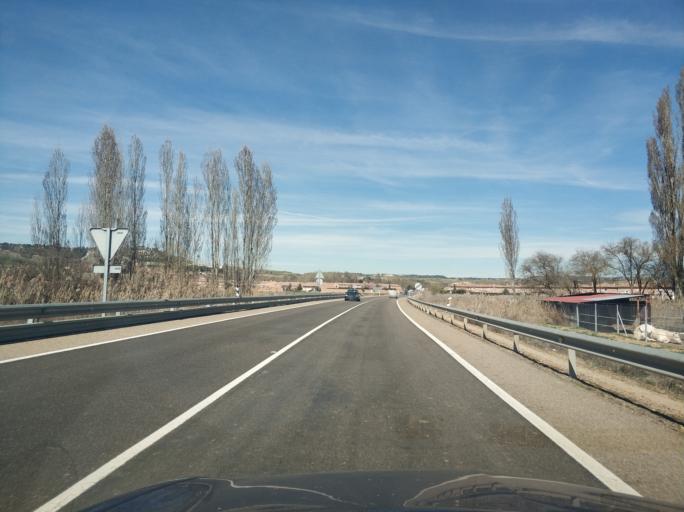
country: ES
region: Castille and Leon
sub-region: Provincia de Valladolid
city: Simancas
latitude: 41.5826
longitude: -4.8159
